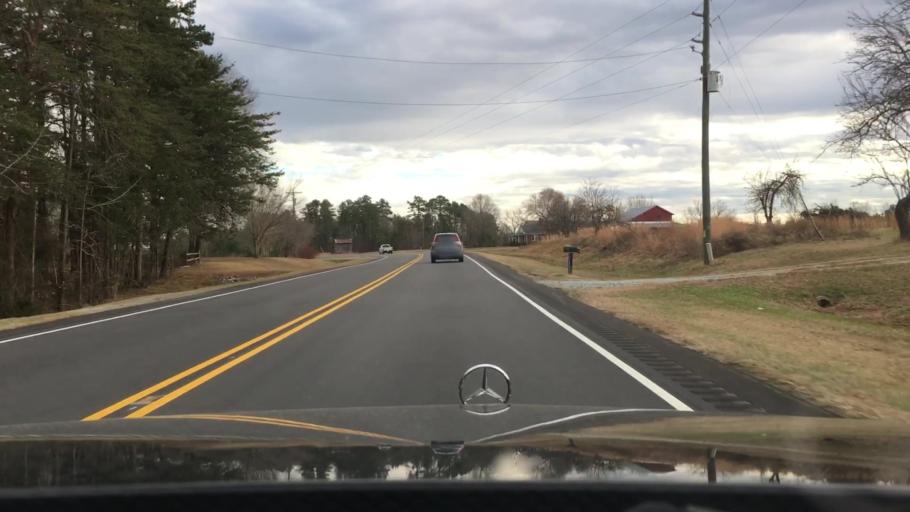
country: US
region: North Carolina
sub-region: Caswell County
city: Yanceyville
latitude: 36.2772
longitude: -79.2076
